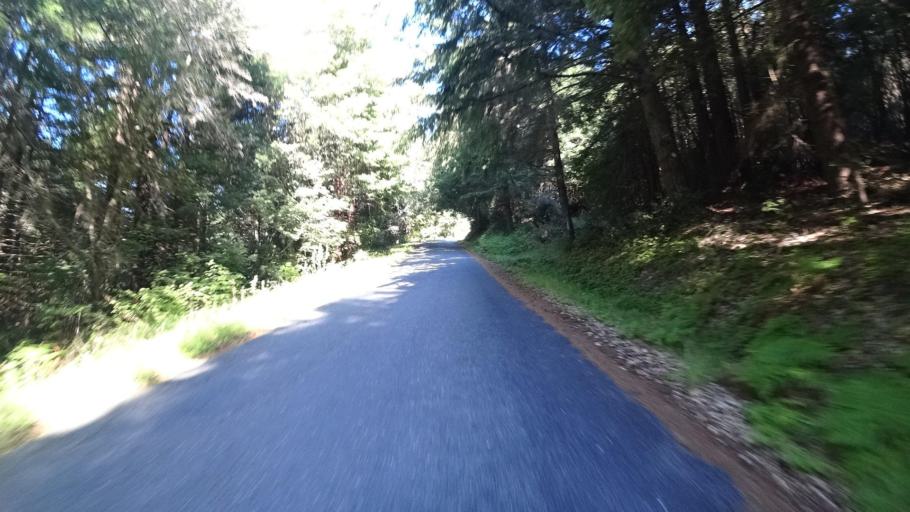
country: US
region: California
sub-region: Humboldt County
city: Rio Dell
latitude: 40.4441
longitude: -123.9736
